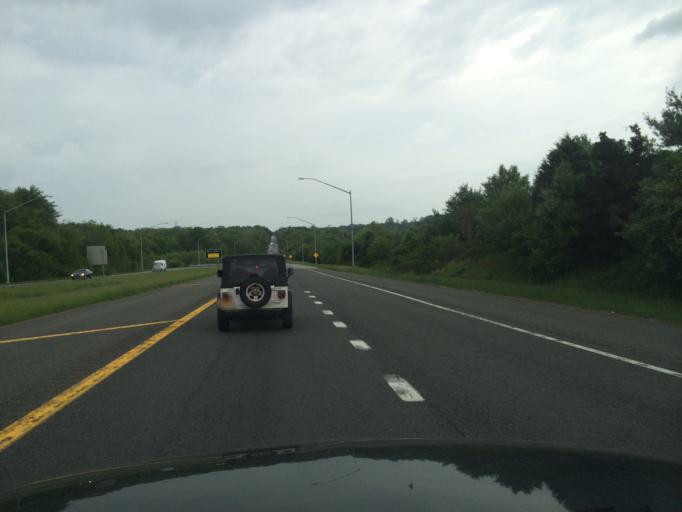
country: US
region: Maryland
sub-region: Howard County
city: Highland
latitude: 39.2101
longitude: -76.9463
